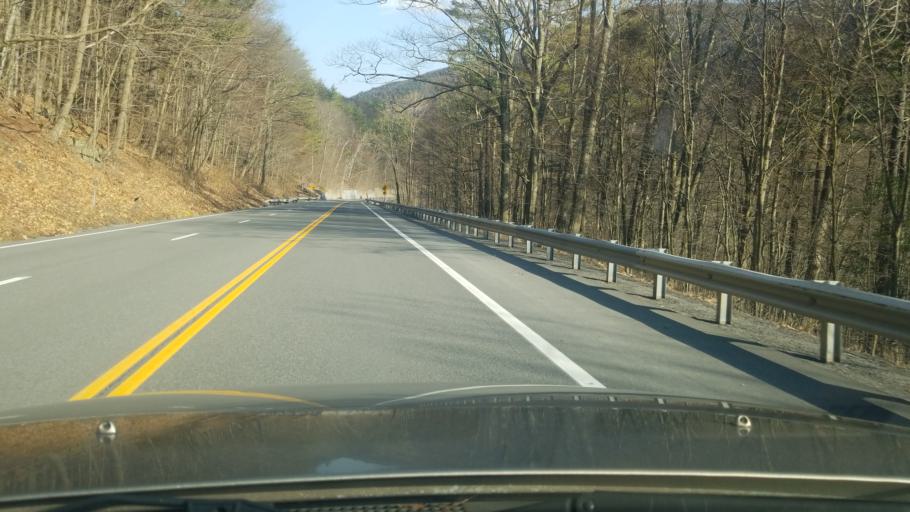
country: US
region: New York
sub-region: Greene County
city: Palenville
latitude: 42.1826
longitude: -74.0654
